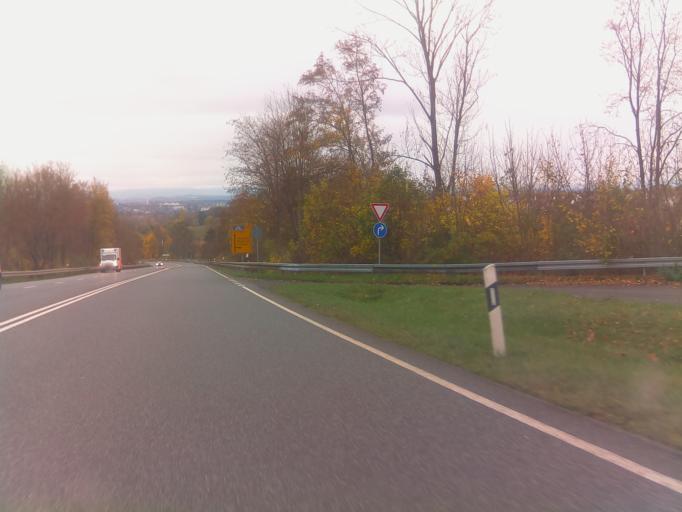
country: DE
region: Hesse
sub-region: Regierungsbezirk Kassel
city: Fulda
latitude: 50.5663
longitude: 9.6249
